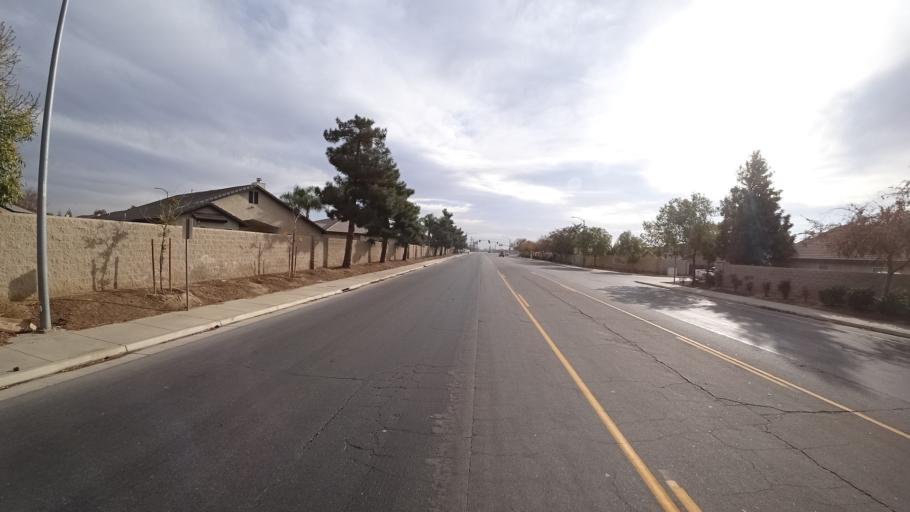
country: US
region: California
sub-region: Kern County
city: Rosedale
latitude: 35.4070
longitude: -119.1455
